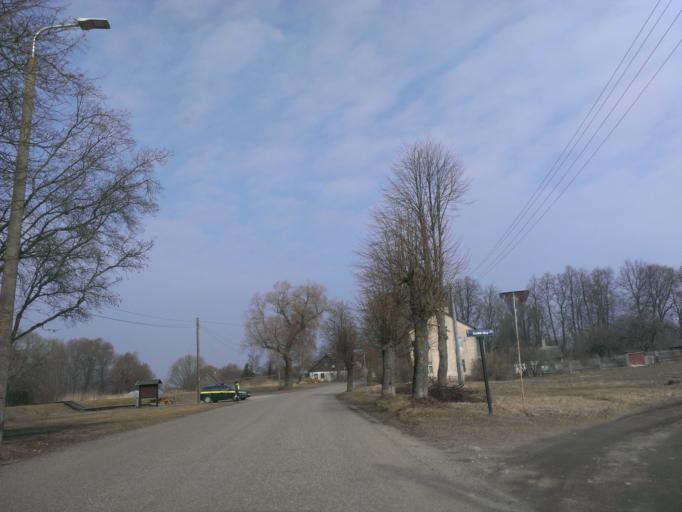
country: LV
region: Salacgrivas
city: Ainazi
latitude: 57.8734
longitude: 24.3609
